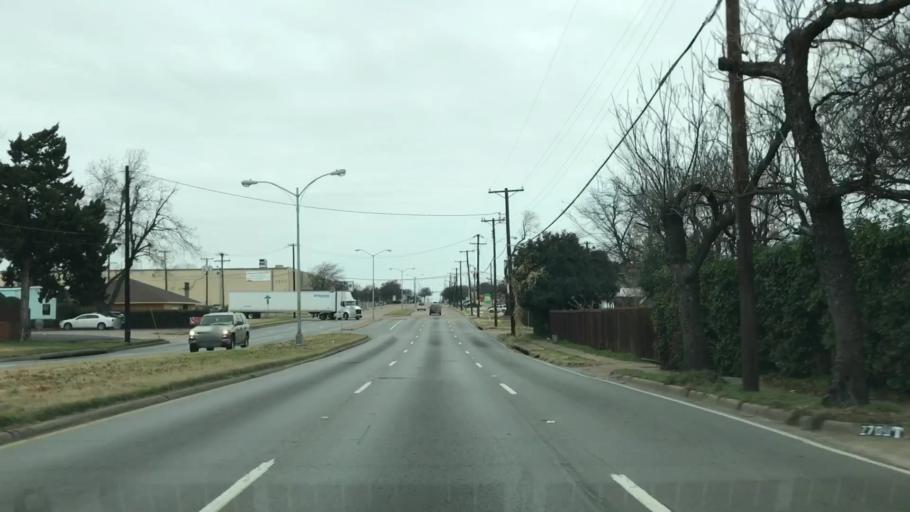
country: US
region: Texas
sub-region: Dallas County
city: Cockrell Hill
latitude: 32.7204
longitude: -96.8644
